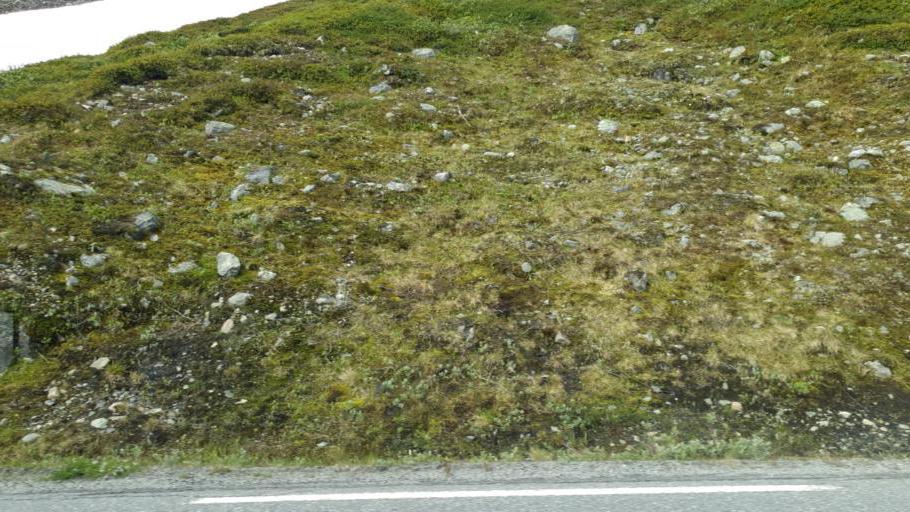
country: NO
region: Oppland
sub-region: Vestre Slidre
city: Slidre
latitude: 61.3389
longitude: 8.8152
